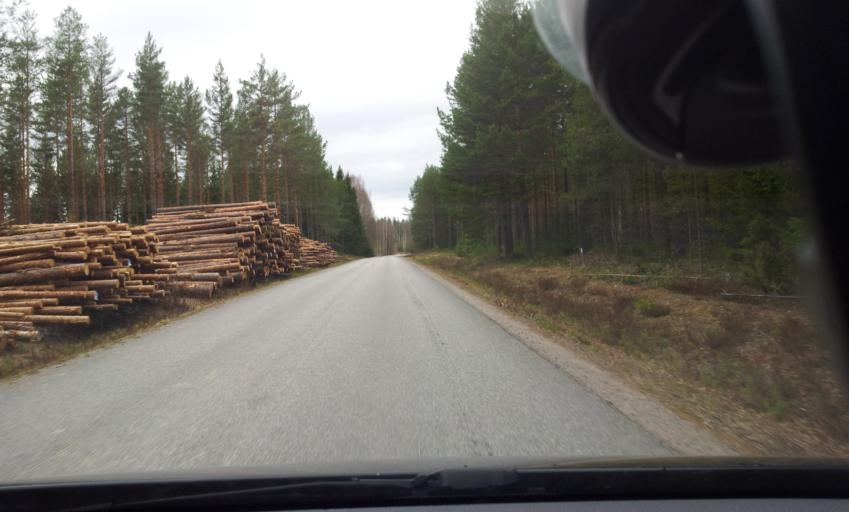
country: SE
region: Gaevleborg
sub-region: Ljusdals Kommun
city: Ljusdal
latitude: 61.8273
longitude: 15.9967
